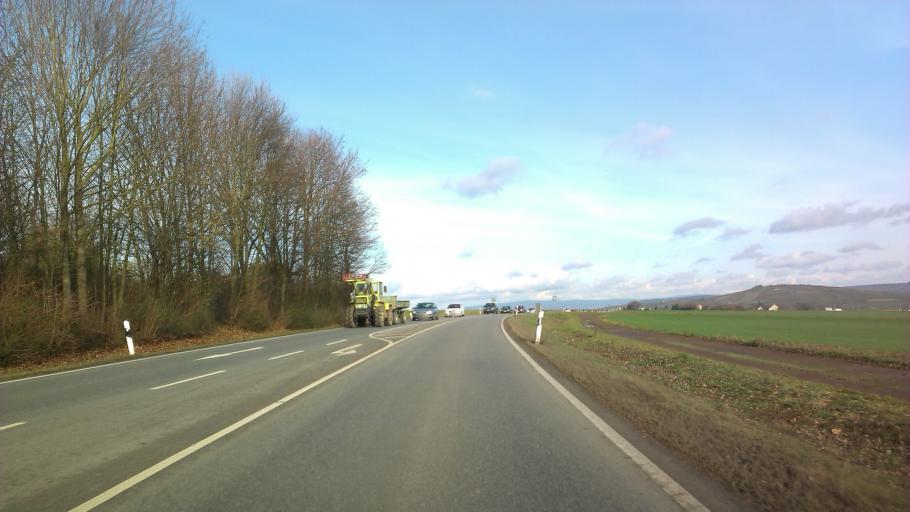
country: DE
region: Rheinland-Pfalz
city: Hackenheim
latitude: 49.8313
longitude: 7.9053
